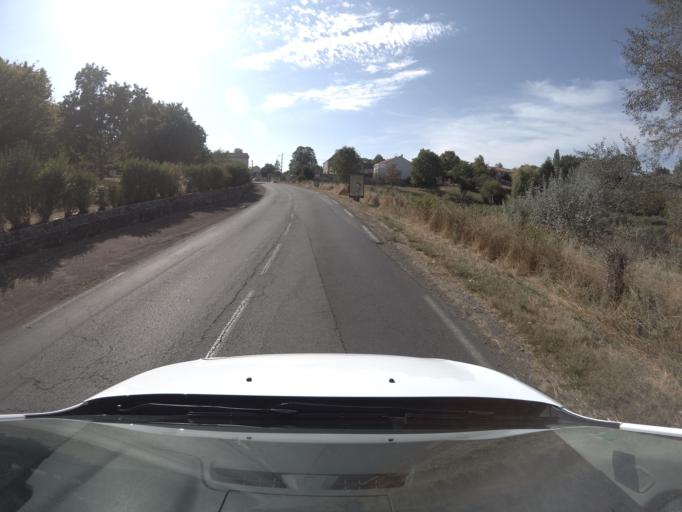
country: FR
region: Poitou-Charentes
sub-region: Departement des Deux-Sevres
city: Mauze-Thouarsais
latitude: 47.0071
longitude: -0.3421
